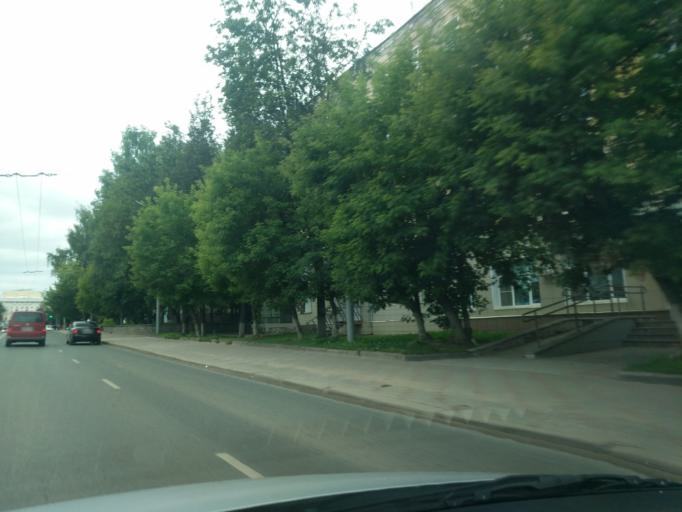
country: RU
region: Kirov
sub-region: Kirovo-Chepetskiy Rayon
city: Kirov
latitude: 58.6097
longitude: 49.6675
